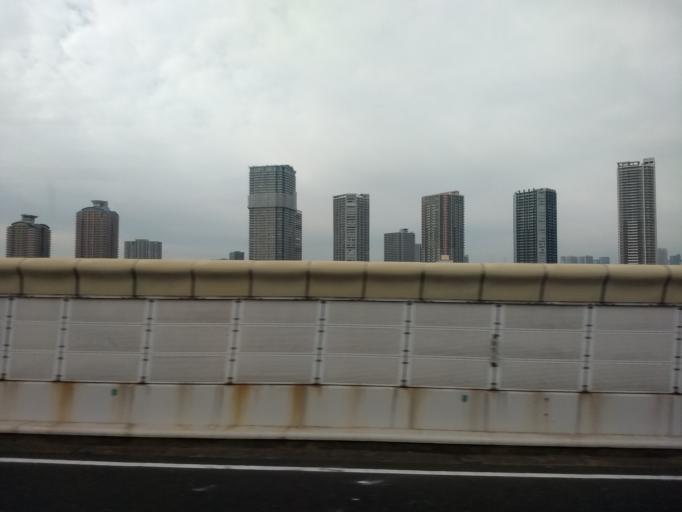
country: JP
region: Tokyo
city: Urayasu
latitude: 35.6473
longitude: 139.8122
